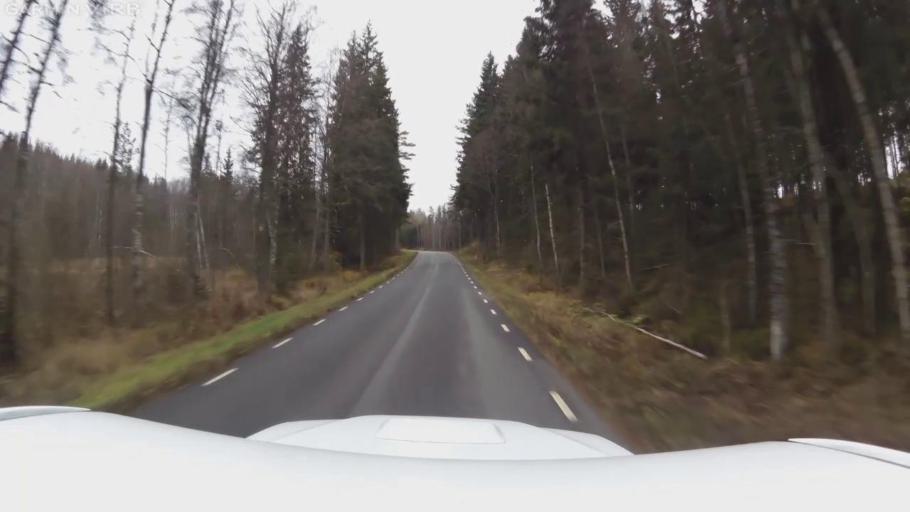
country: SE
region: OEstergoetland
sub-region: Mjolby Kommun
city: Mantorp
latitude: 58.1676
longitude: 15.3972
